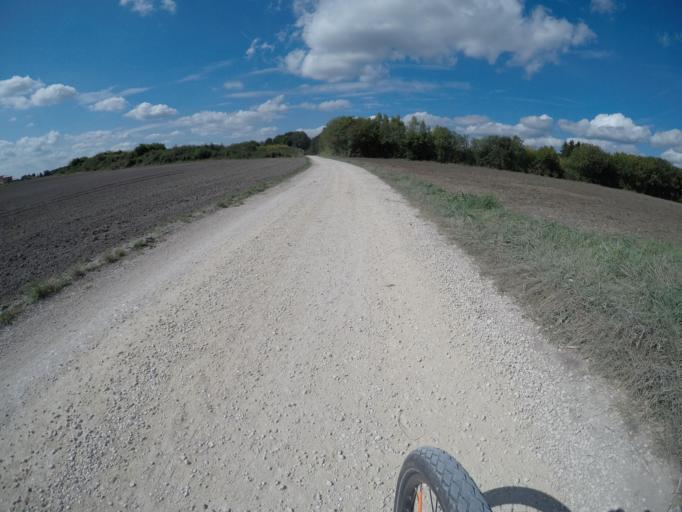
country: DE
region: Bavaria
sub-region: Swabia
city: Wittislingen
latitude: 48.6129
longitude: 10.4299
